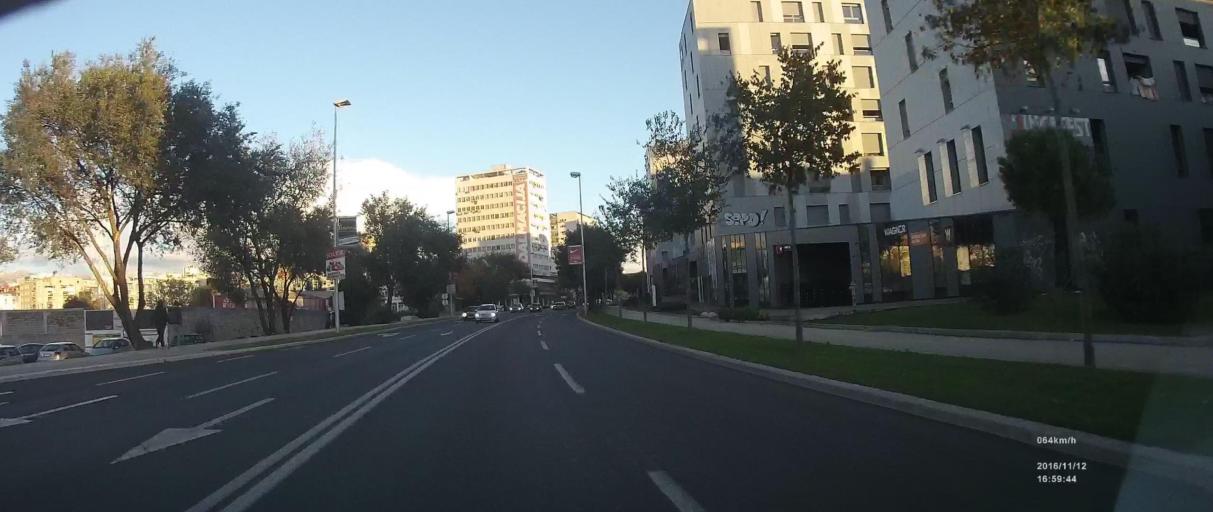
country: HR
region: Splitsko-Dalmatinska
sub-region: Grad Split
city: Split
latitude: 43.5183
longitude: 16.4425
